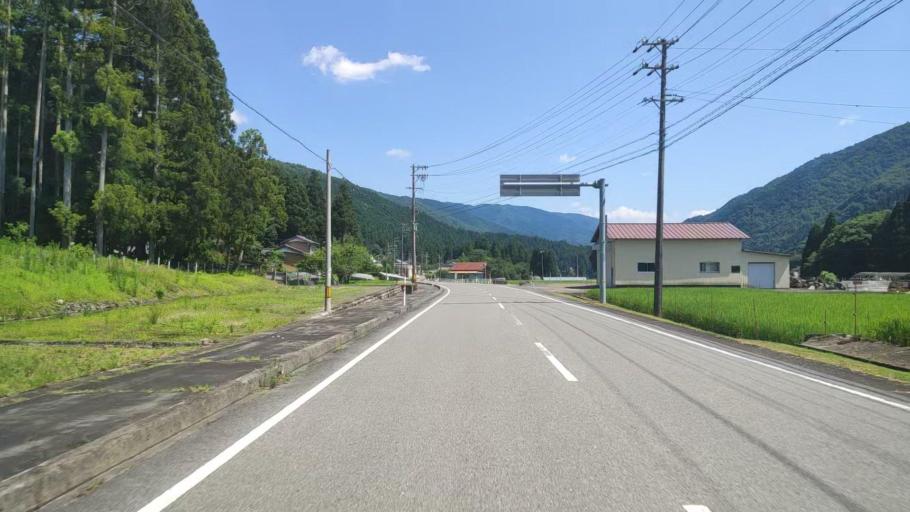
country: JP
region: Gifu
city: Godo
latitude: 35.6497
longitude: 136.5973
